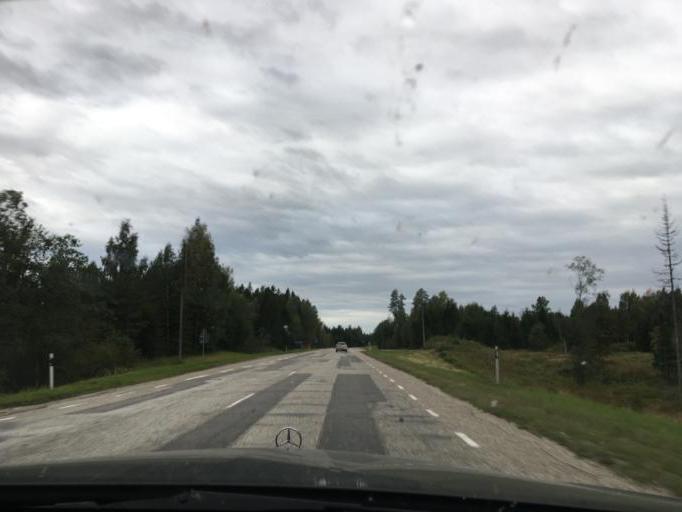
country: LV
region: Aluksnes Rajons
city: Aluksne
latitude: 57.5894
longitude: 27.0796
